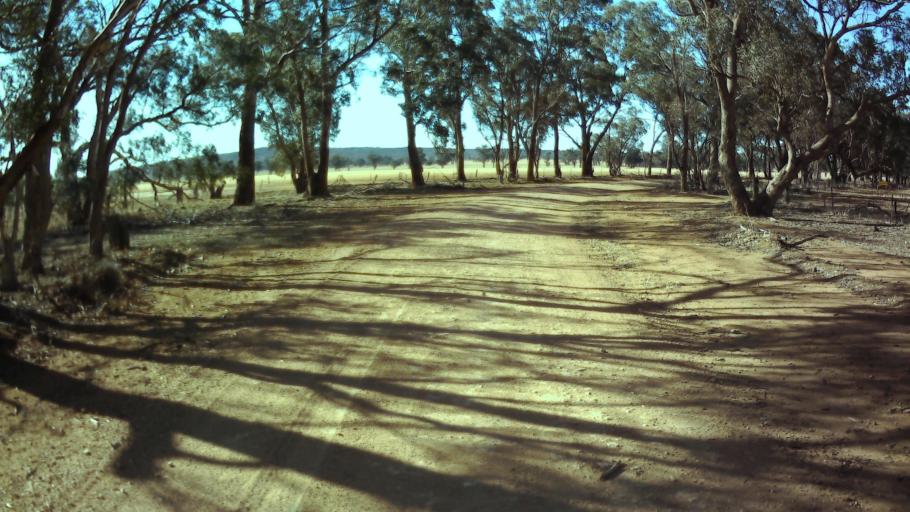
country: AU
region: New South Wales
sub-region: Weddin
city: Grenfell
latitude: -33.8358
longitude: 147.8730
